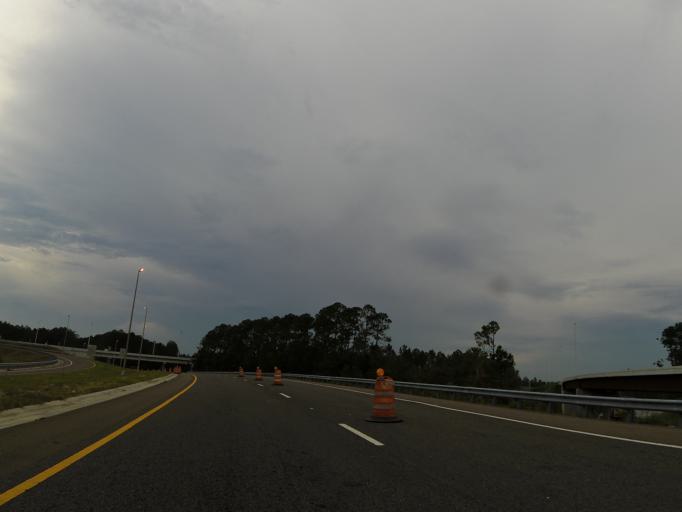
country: US
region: Florida
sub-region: Duval County
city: Baldwin
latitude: 30.3102
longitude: -81.8754
